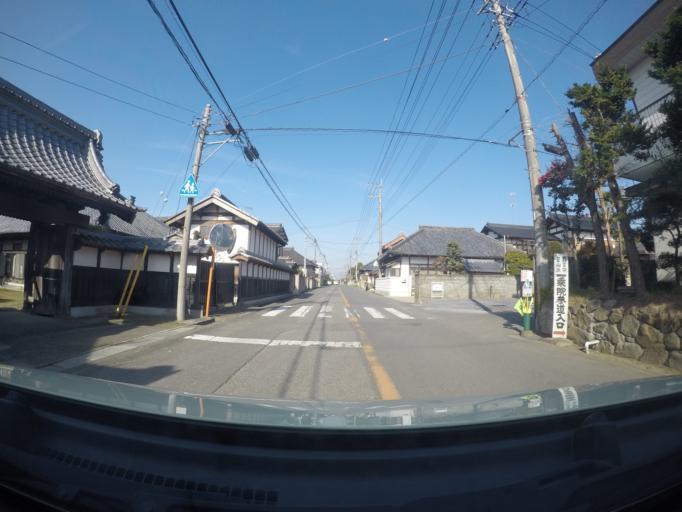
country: JP
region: Ibaraki
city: Tsukuba
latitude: 36.2213
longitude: 140.0664
